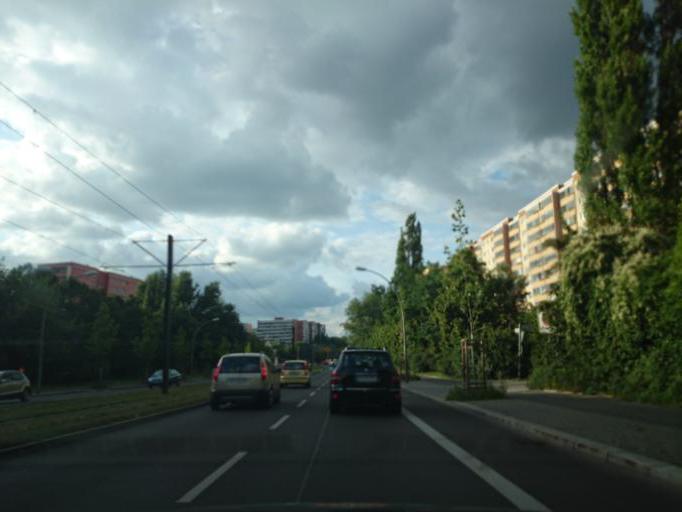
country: DE
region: Berlin
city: Friedrichsfelde
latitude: 52.5067
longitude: 13.5197
